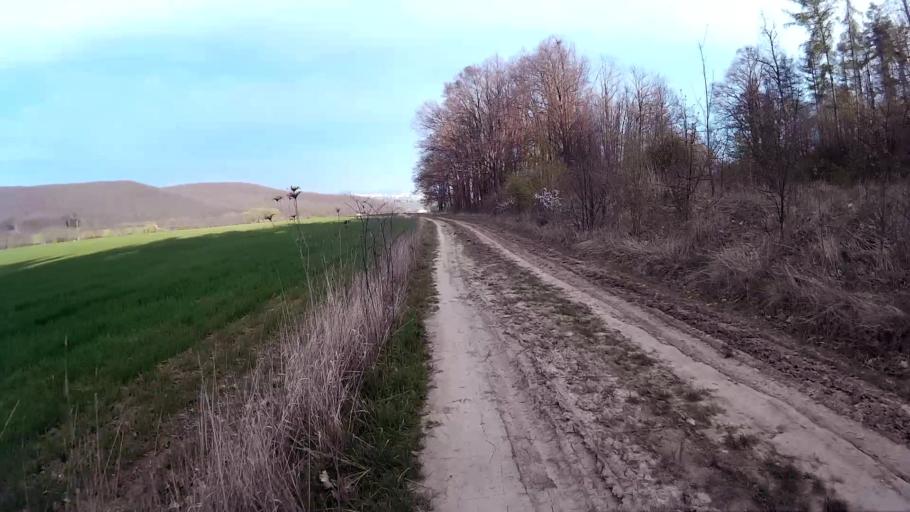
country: CZ
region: South Moravian
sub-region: Mesto Brno
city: Mokra Hora
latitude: 49.2453
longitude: 16.5411
